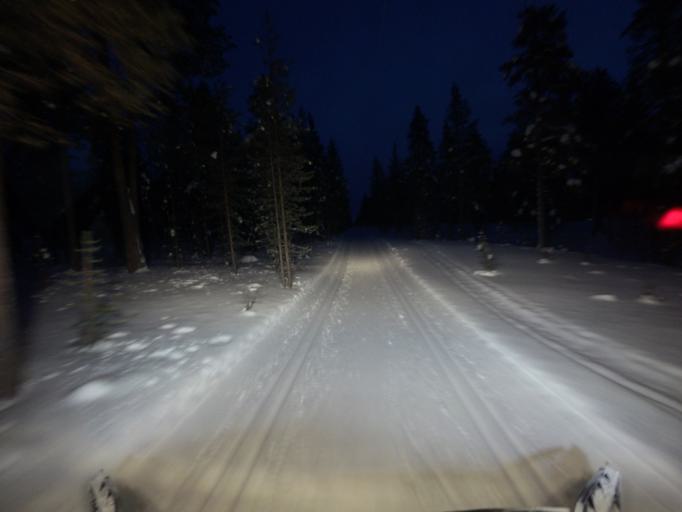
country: FI
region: Lapland
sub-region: Tunturi-Lappi
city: Kolari
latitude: 67.5933
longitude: 24.1049
